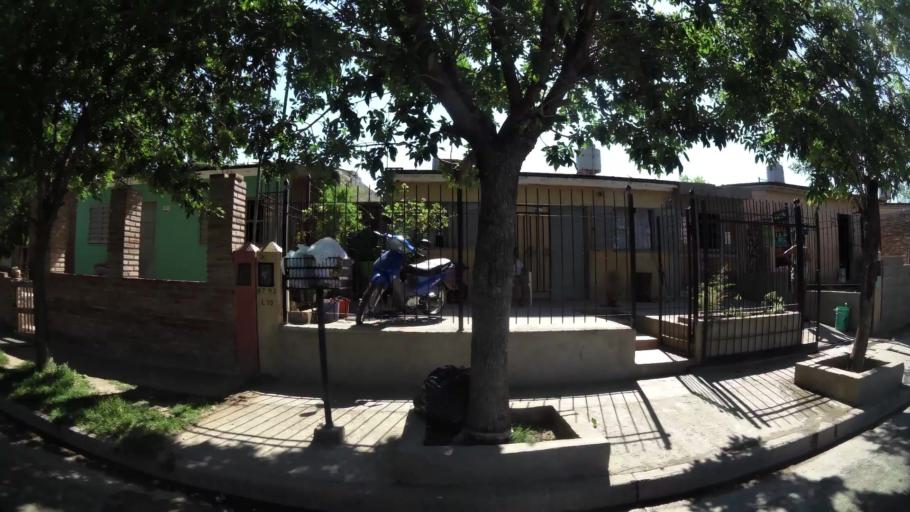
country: AR
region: Cordoba
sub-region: Departamento de Capital
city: Cordoba
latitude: -31.4132
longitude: -64.1435
